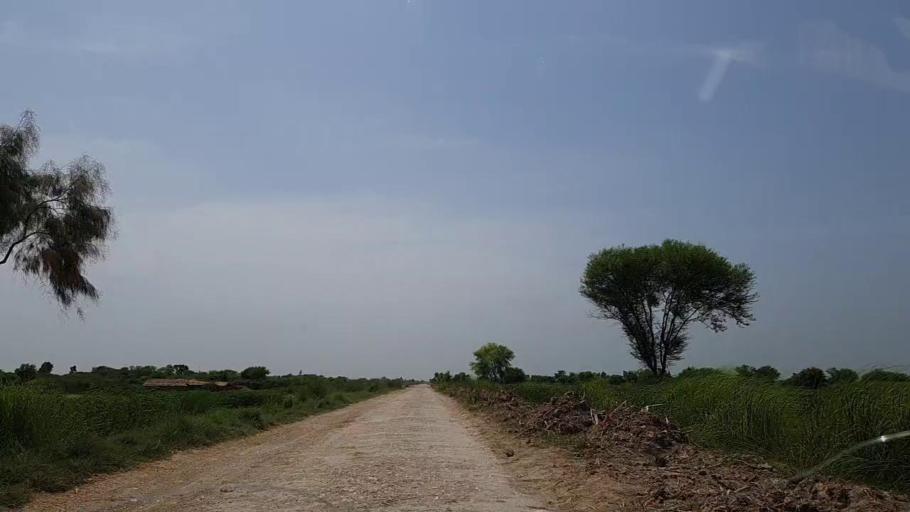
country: PK
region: Sindh
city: Khanpur
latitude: 27.8785
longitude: 69.4917
